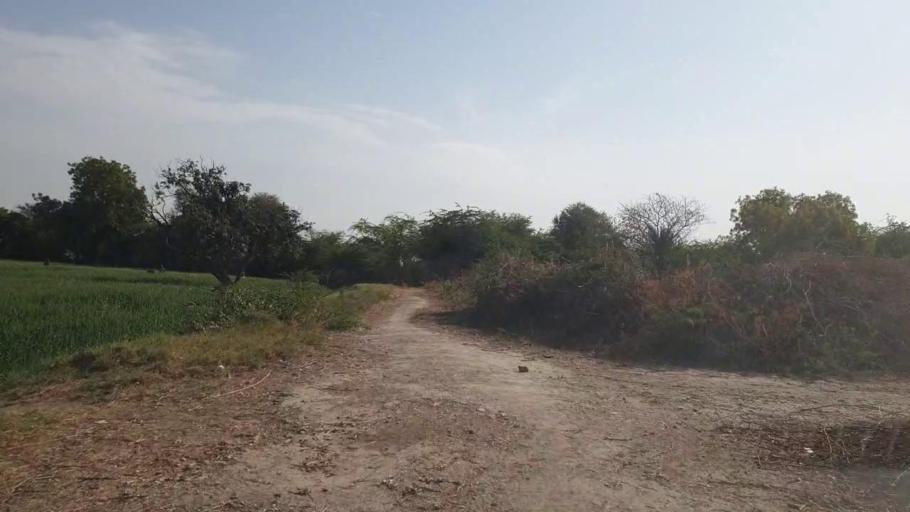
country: PK
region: Sindh
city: Dhoro Naro
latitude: 25.4498
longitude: 69.5400
